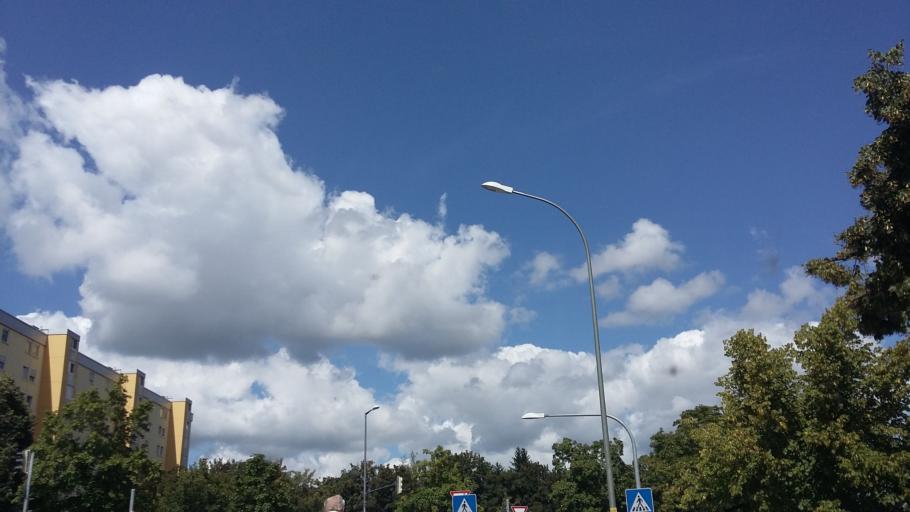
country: DE
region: Bavaria
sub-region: Upper Bavaria
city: Pasing
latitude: 48.1490
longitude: 11.4344
